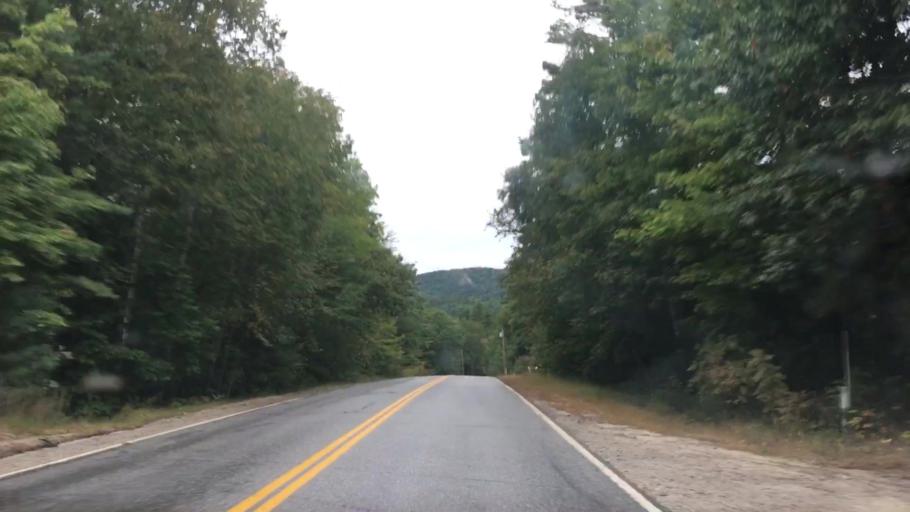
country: US
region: Maine
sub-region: Cumberland County
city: Raymond
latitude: 43.9442
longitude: -70.4592
